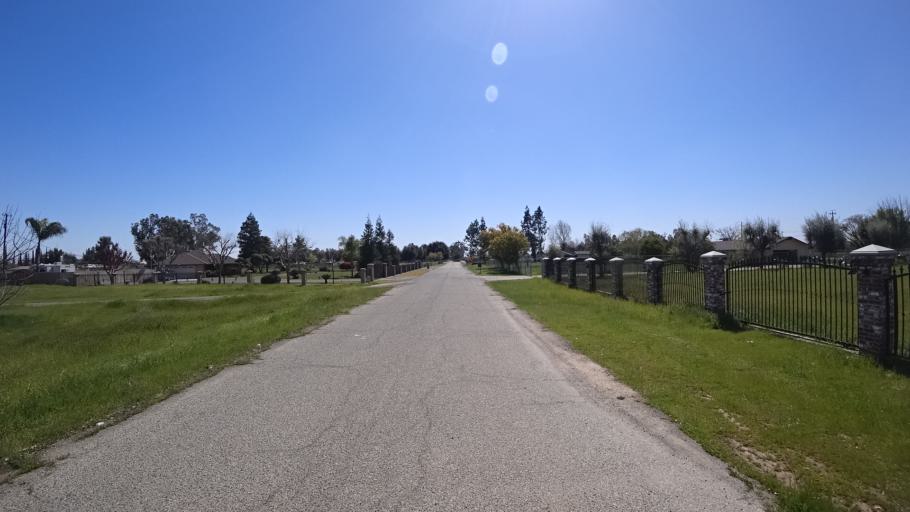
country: US
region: California
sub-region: Fresno County
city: West Park
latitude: 36.7668
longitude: -119.8657
